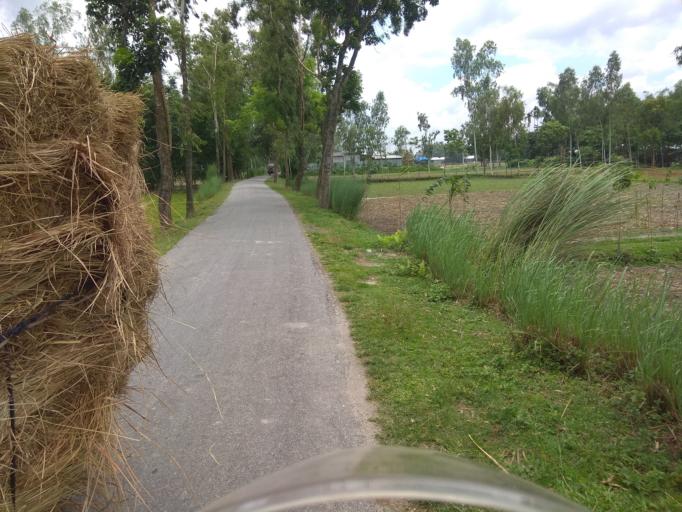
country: IN
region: West Bengal
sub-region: Koch Bihar
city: Haldibari
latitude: 26.2417
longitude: 88.8922
